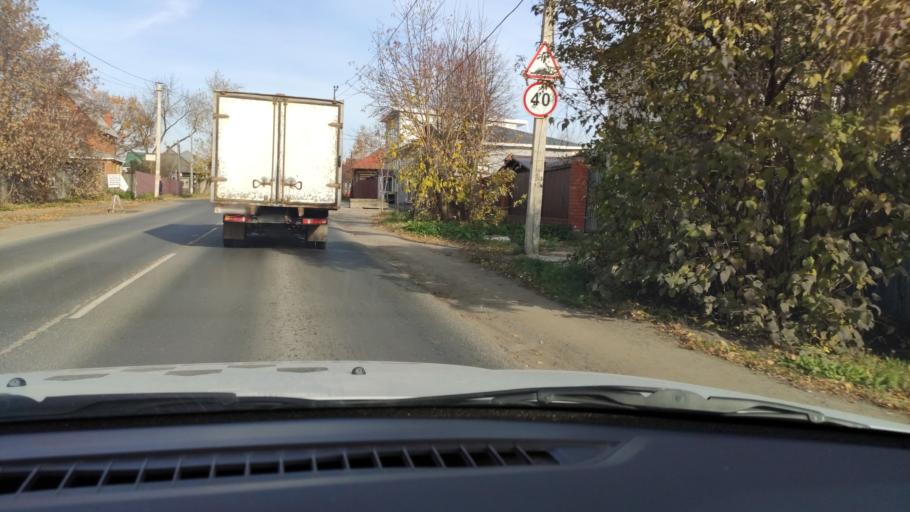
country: RU
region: Perm
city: Perm
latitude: 58.0354
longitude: 56.3421
